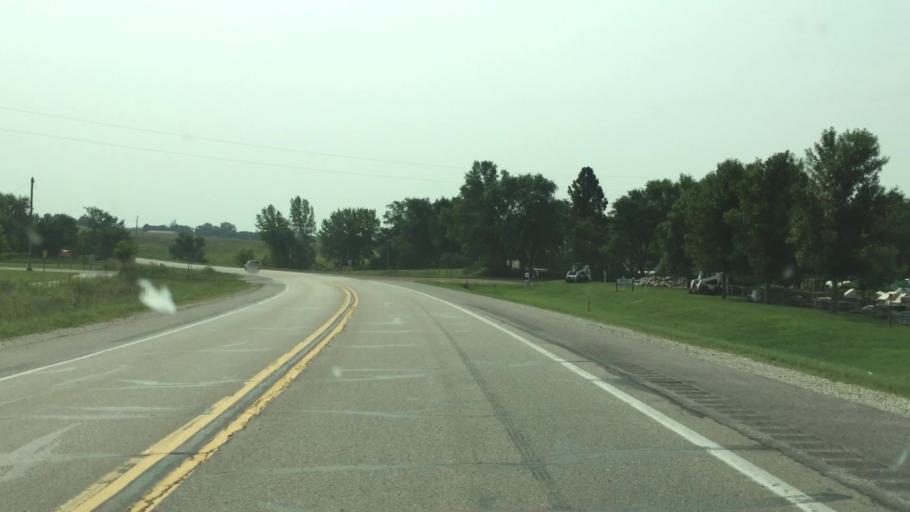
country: US
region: Iowa
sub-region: Dickinson County
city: Milford
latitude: 43.3442
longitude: -95.1785
